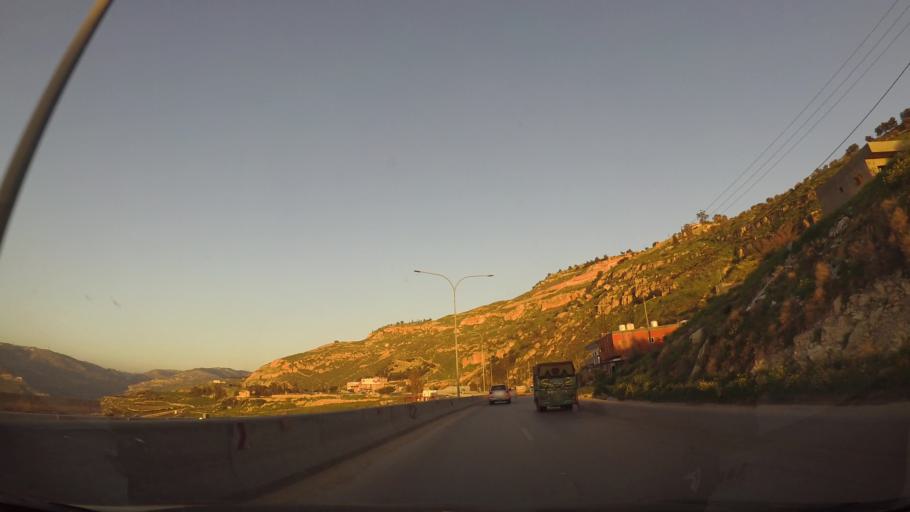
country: JO
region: Amman
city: Umm as Summaq
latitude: 31.8678
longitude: 35.7650
